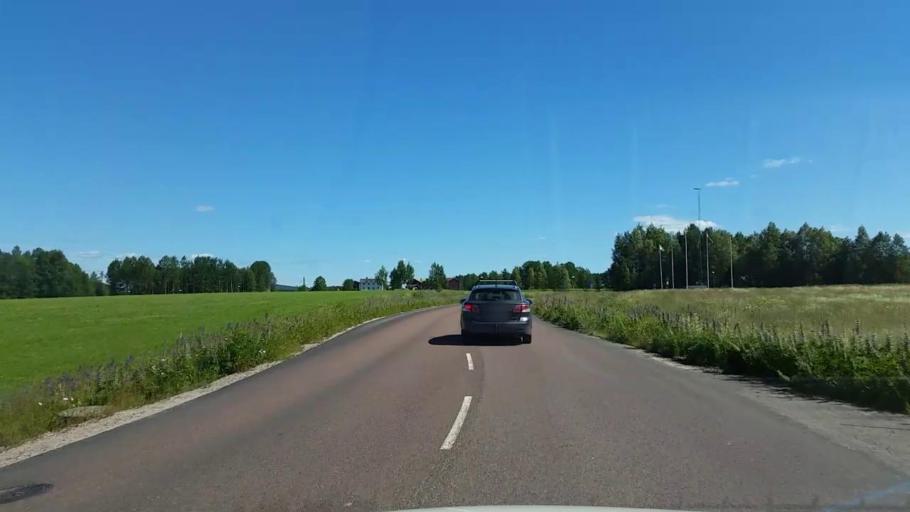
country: SE
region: Gaevleborg
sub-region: Ovanakers Kommun
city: Edsbyn
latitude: 61.3692
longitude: 15.8180
